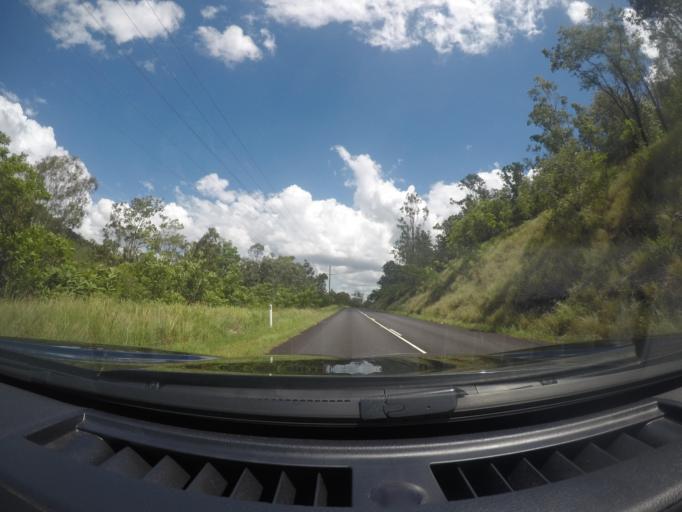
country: AU
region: Queensland
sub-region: Moreton Bay
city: Woodford
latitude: -27.1308
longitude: 152.5538
